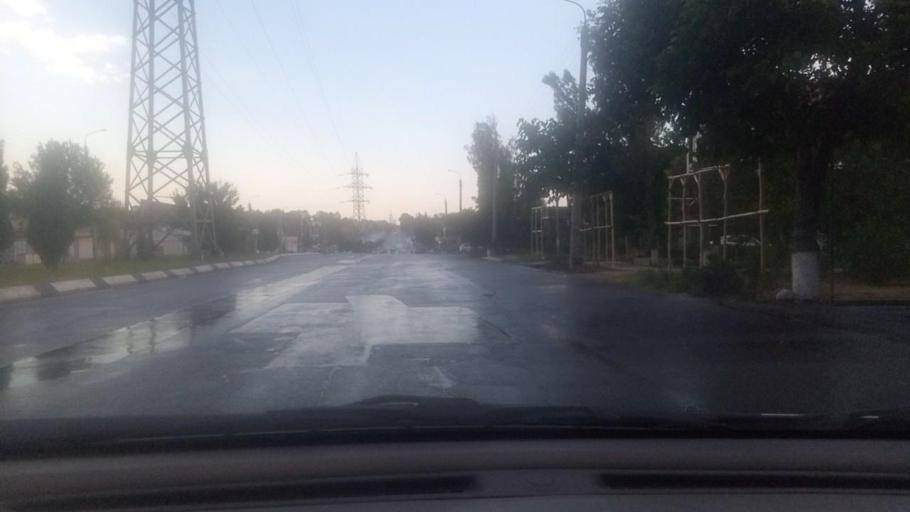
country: UZ
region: Toshkent Shahri
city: Tashkent
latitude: 41.3079
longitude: 69.1935
